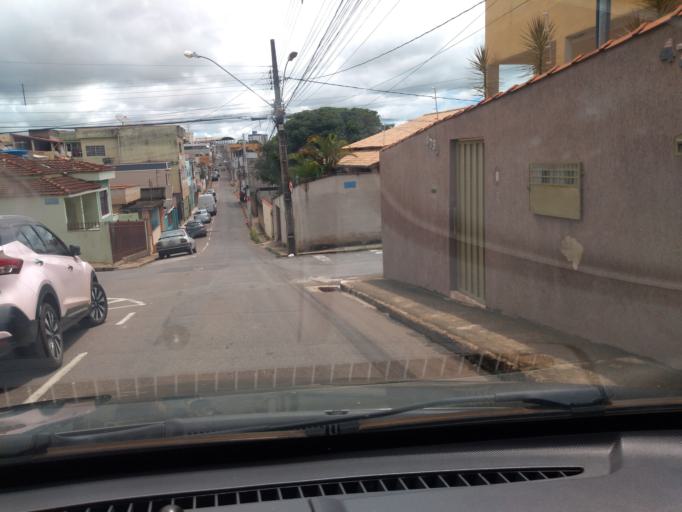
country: BR
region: Minas Gerais
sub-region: Tres Coracoes
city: Tres Coracoes
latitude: -21.6899
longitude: -45.2535
